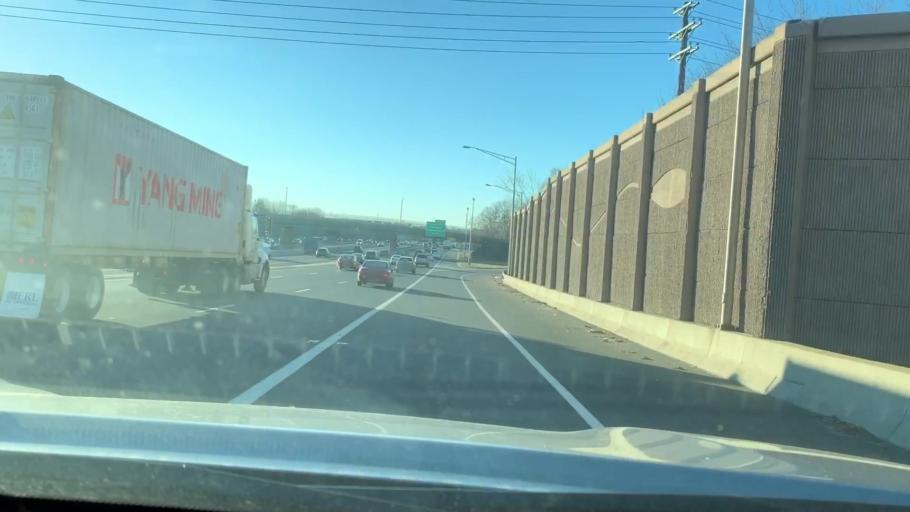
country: US
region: New Jersey
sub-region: Bergen County
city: Bogota
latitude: 40.8672
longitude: -74.0403
